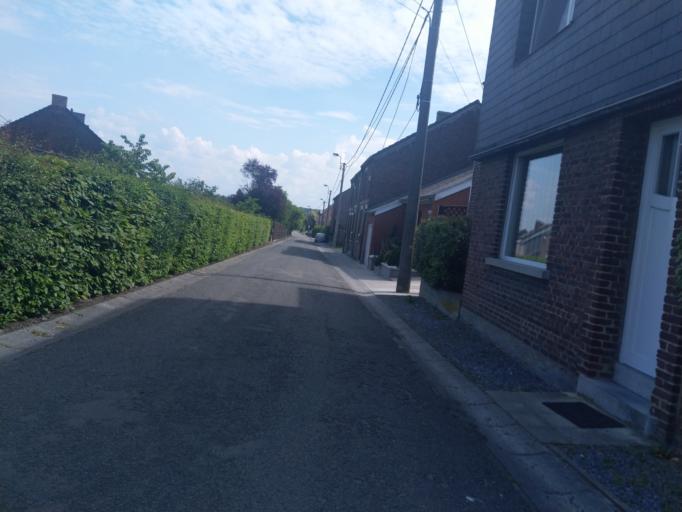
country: BE
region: Wallonia
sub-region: Province du Hainaut
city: Mons
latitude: 50.4473
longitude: 3.9936
